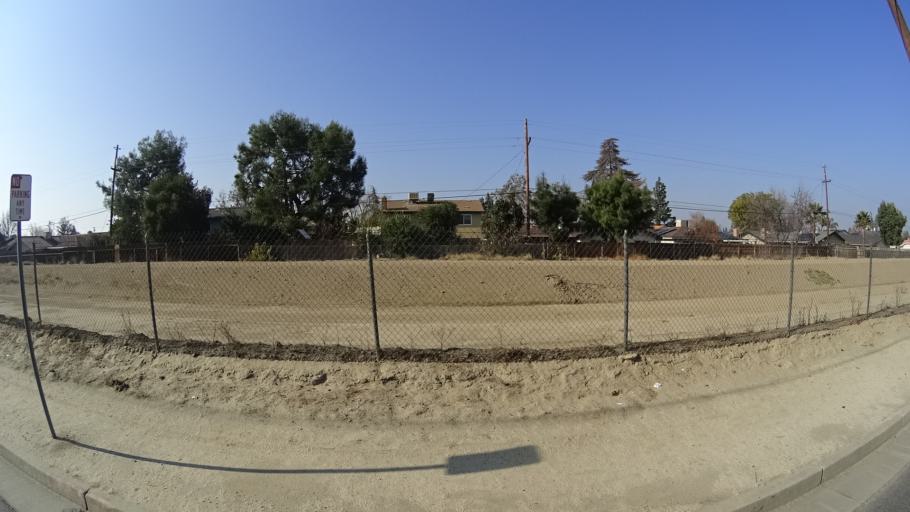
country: US
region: California
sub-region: Kern County
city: Bakersfield
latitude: 35.3339
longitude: -119.0555
